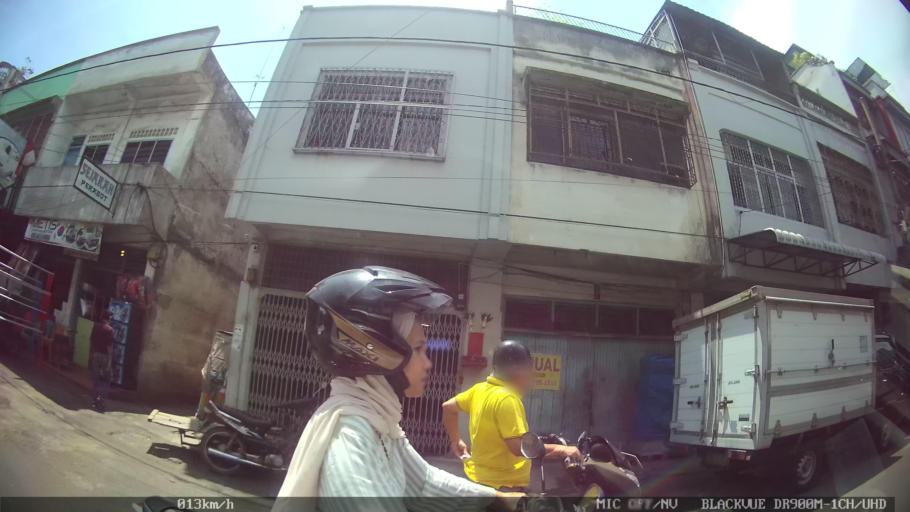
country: ID
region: North Sumatra
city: Binjai
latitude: 3.6066
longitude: 98.4892
